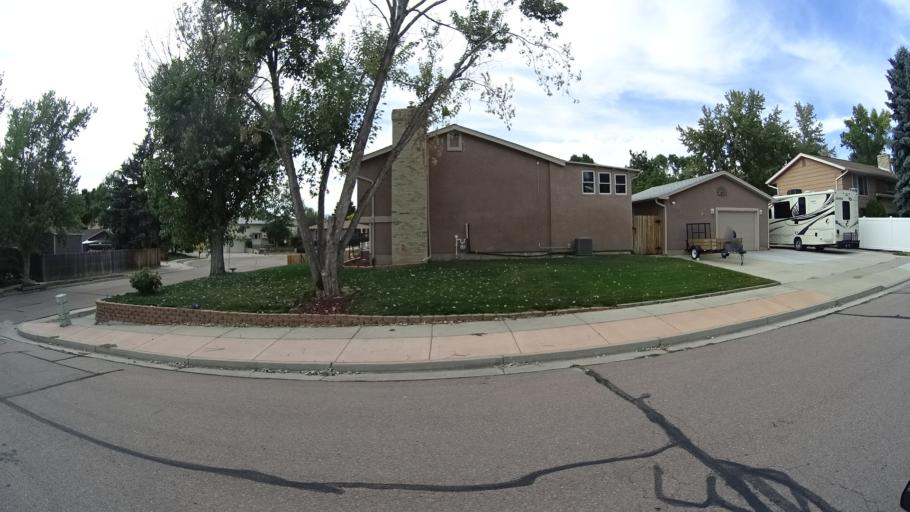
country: US
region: Colorado
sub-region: El Paso County
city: Colorado Springs
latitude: 38.9006
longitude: -104.7736
